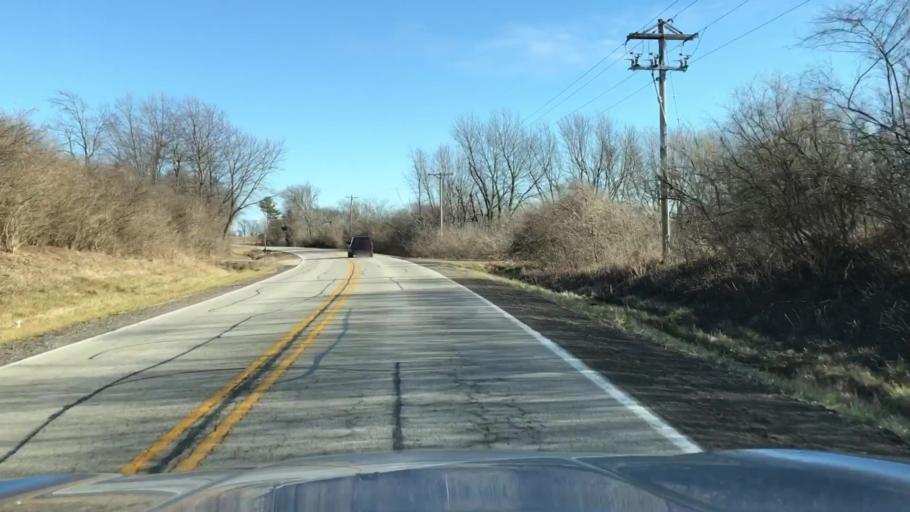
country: US
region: Illinois
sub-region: McLean County
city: Lexington
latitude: 40.6452
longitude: -88.8353
